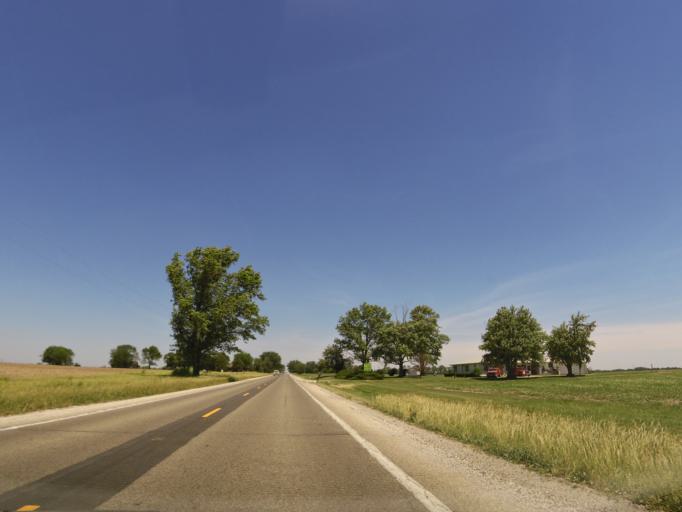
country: US
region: Illinois
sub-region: Vermilion County
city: Hoopeston
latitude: 40.4289
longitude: -87.6858
